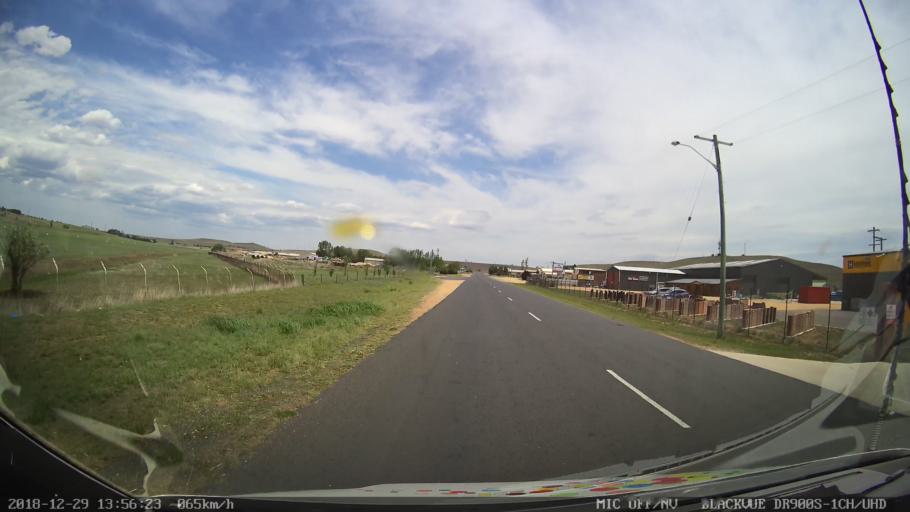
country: AU
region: New South Wales
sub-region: Cooma-Monaro
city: Cooma
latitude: -36.2301
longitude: 149.1463
